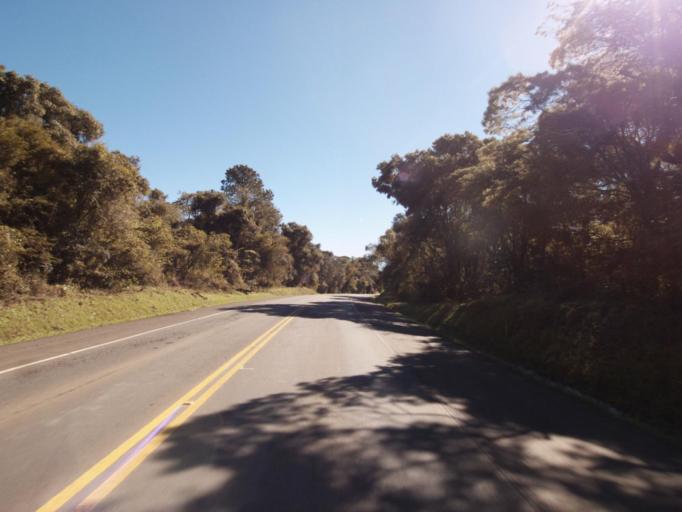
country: BR
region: Santa Catarina
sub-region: Joacaba
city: Joacaba
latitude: -27.1229
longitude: -51.6316
